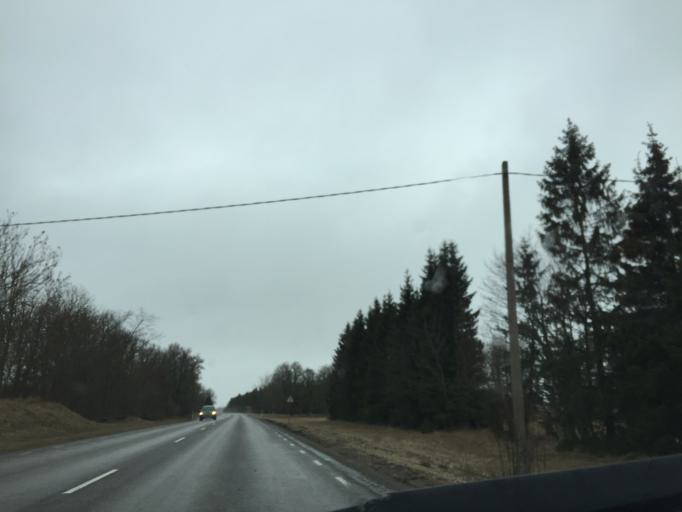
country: EE
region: Laeaene
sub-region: Ridala Parish
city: Uuemoisa
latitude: 58.8771
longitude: 23.6095
